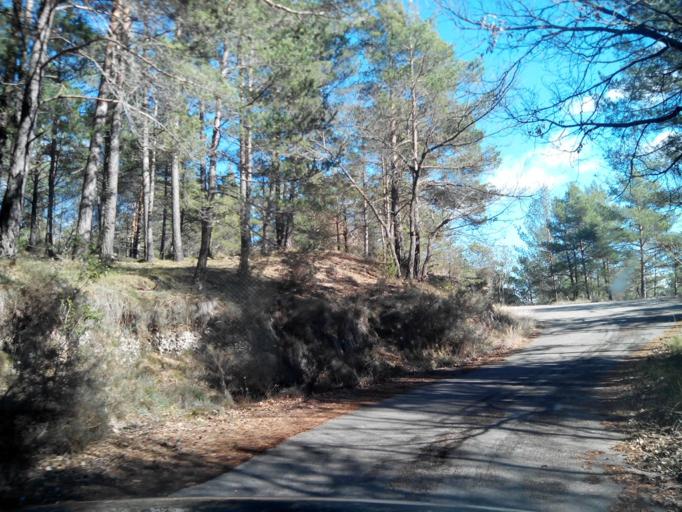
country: ES
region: Catalonia
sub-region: Provincia de Barcelona
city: Vilada
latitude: 42.1305
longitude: 1.9281
